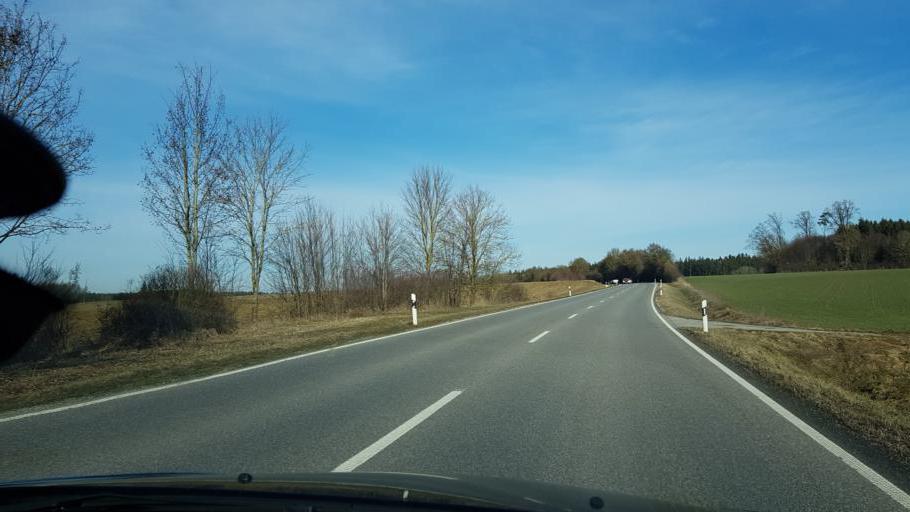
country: DE
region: Bavaria
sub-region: Upper Bavaria
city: Hattenhofen
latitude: 48.2308
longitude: 11.1137
